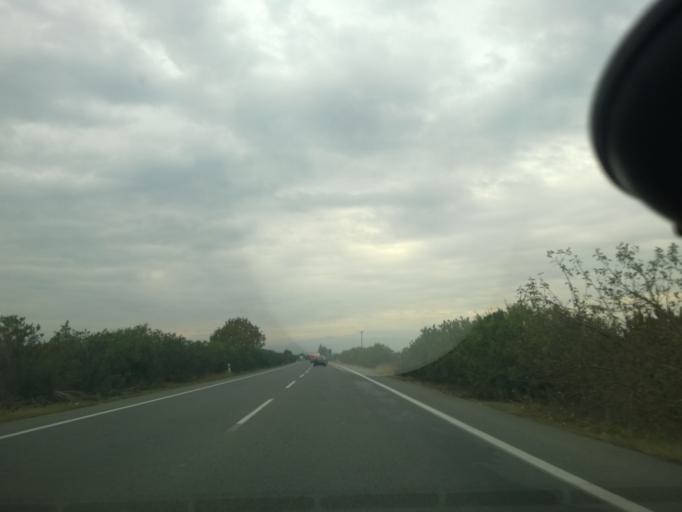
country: GR
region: Central Macedonia
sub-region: Nomos Pellis
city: Palaifyto
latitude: 40.8089
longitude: 22.2322
